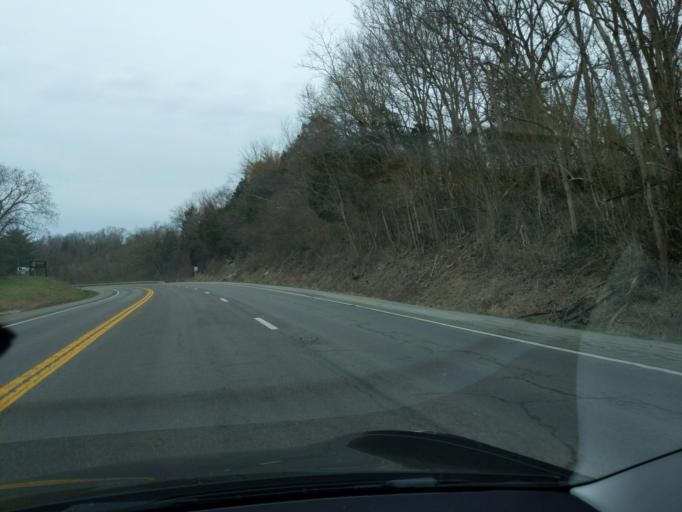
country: US
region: Kentucky
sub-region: Clark County
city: Winchester
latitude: 37.8905
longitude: -84.2822
